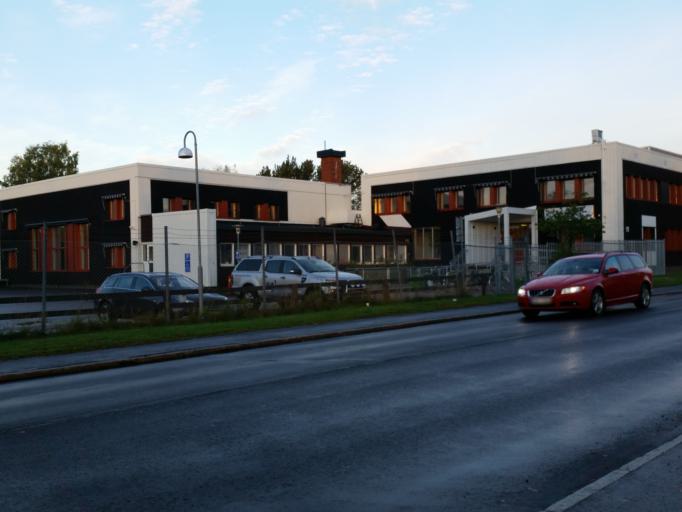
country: SE
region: Norrbotten
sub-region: Lulea Kommun
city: Lulea
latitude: 65.6019
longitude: 22.1388
